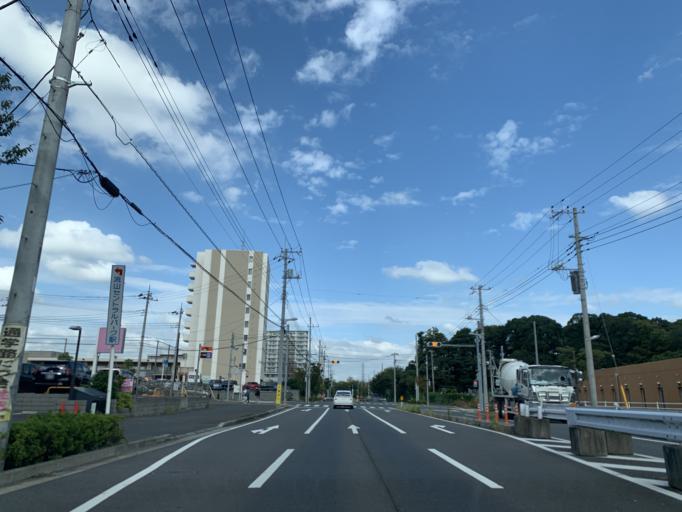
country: JP
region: Chiba
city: Nagareyama
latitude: 35.8534
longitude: 139.9166
